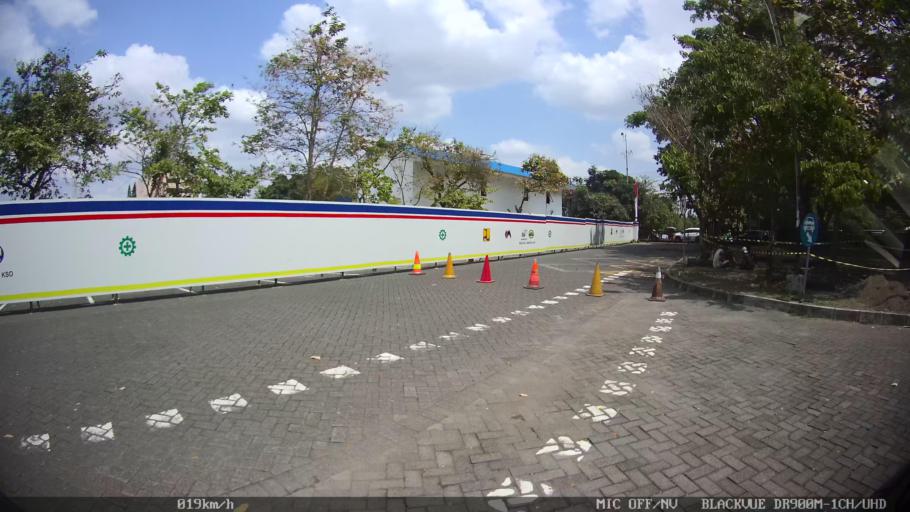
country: ID
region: Daerah Istimewa Yogyakarta
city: Yogyakarta
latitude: -7.7723
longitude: 110.3773
